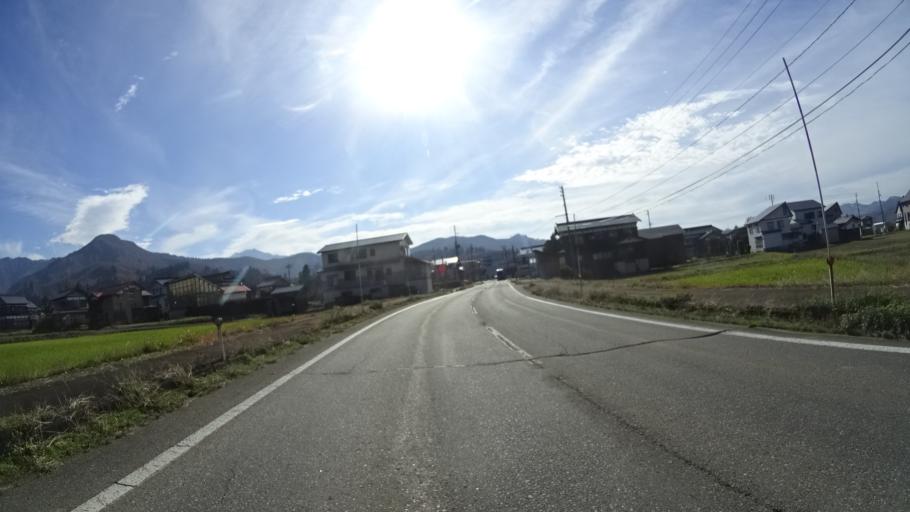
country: JP
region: Niigata
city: Muikamachi
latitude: 37.2126
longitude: 138.9803
